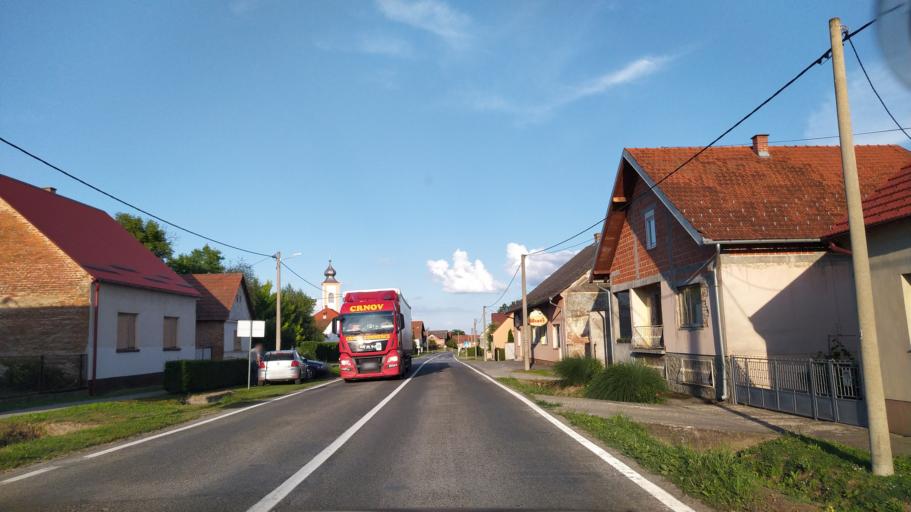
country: HR
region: Virovitick-Podravska
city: Cacinci
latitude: 45.6134
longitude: 17.8057
